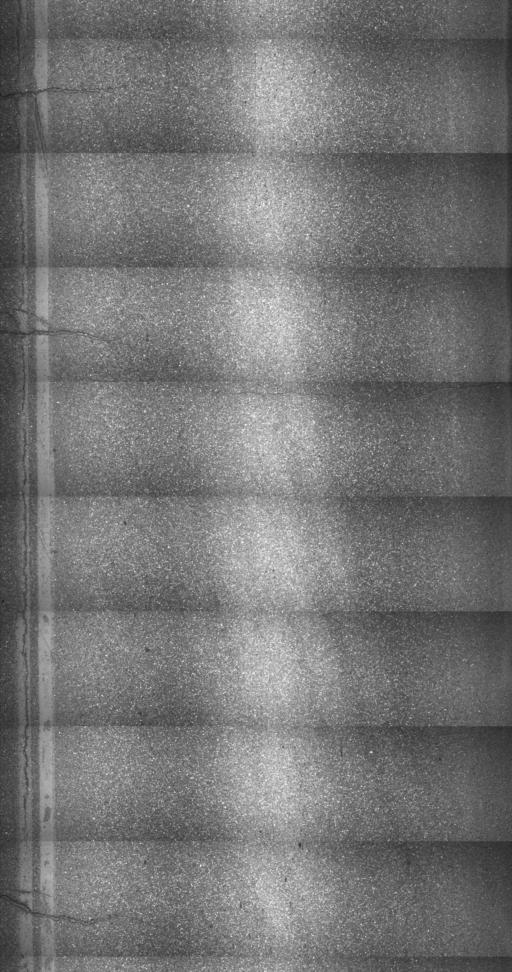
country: US
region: Vermont
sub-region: Lamoille County
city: Johnson
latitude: 44.6255
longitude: -72.6775
